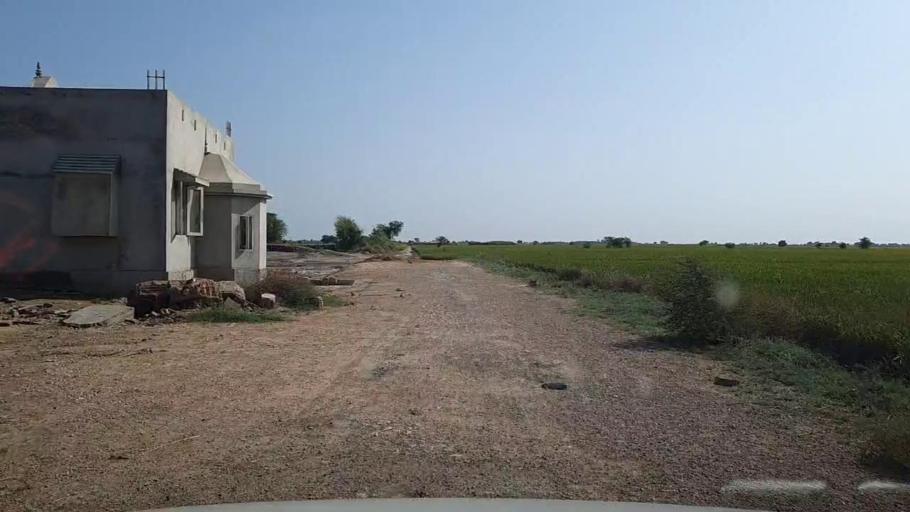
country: PK
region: Sindh
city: Kario
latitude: 24.8282
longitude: 68.5238
